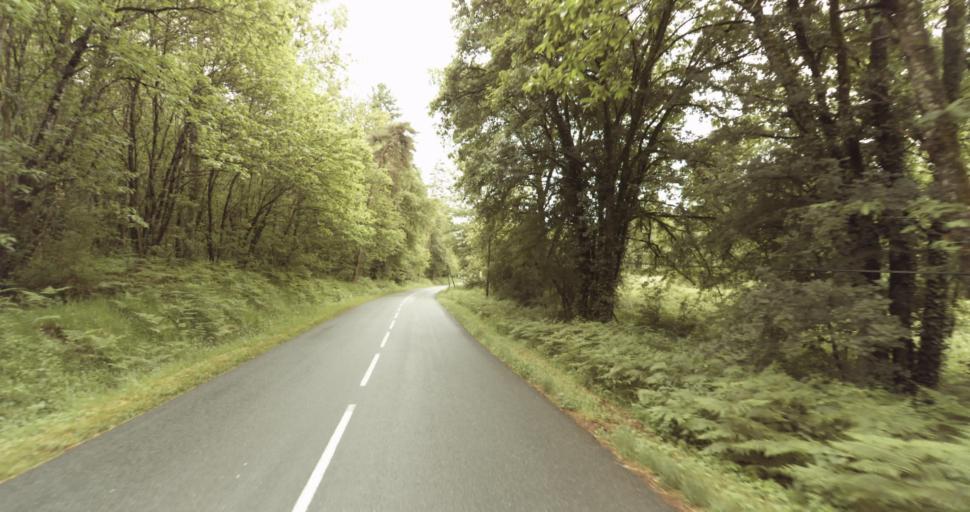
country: FR
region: Aquitaine
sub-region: Departement de la Dordogne
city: Belves
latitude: 44.7138
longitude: 0.9343
